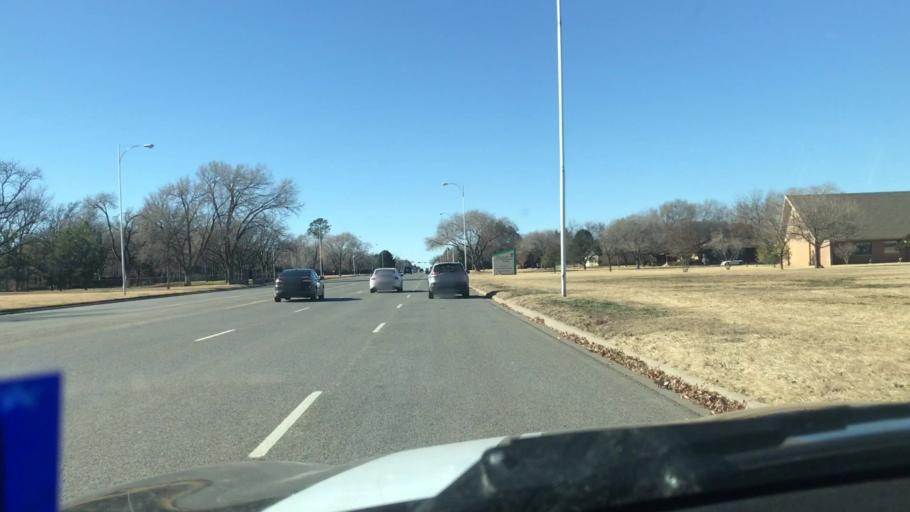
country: US
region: Texas
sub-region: Lubbock County
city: Lubbock
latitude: 33.5779
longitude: -101.9166
